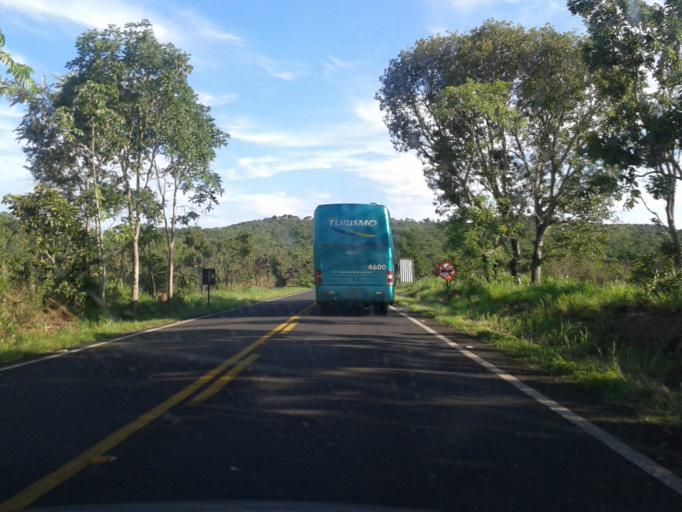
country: BR
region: Minas Gerais
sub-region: Tupaciguara
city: Tupaciguara
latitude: -18.3094
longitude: -48.5614
